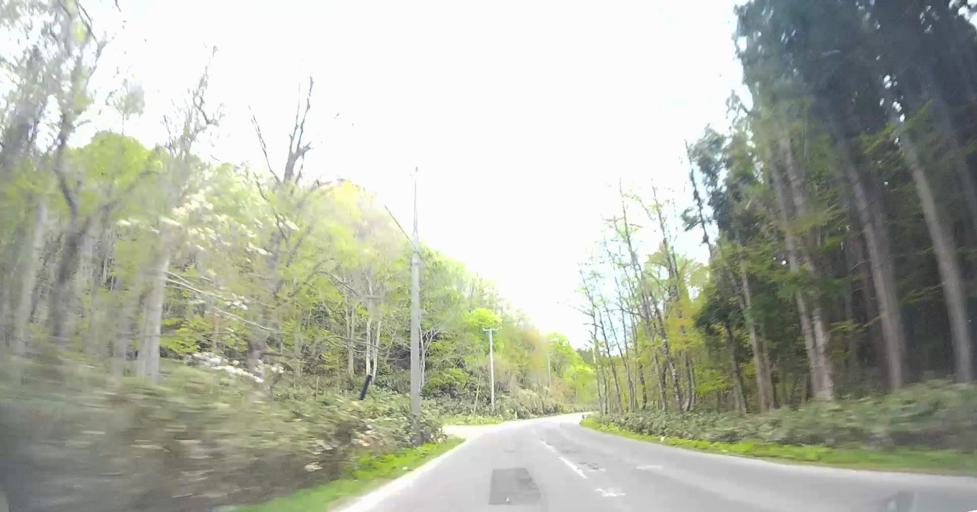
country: JP
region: Aomori
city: Goshogawara
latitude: 41.1168
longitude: 140.5261
